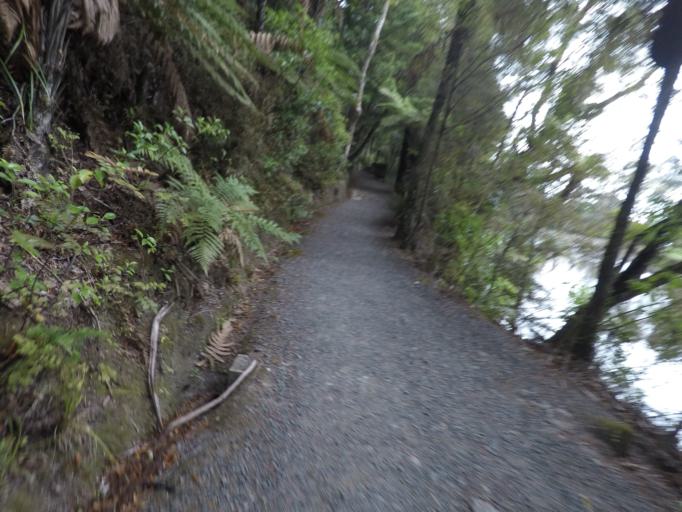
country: NZ
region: Northland
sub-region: Whangarei
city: Whangarei
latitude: -35.7124
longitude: 174.3304
